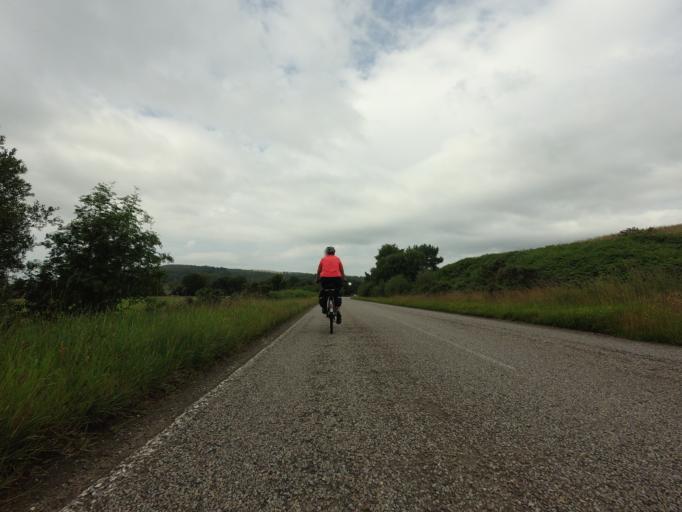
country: GB
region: Scotland
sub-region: Highland
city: Evanton
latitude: 57.9397
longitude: -4.4063
